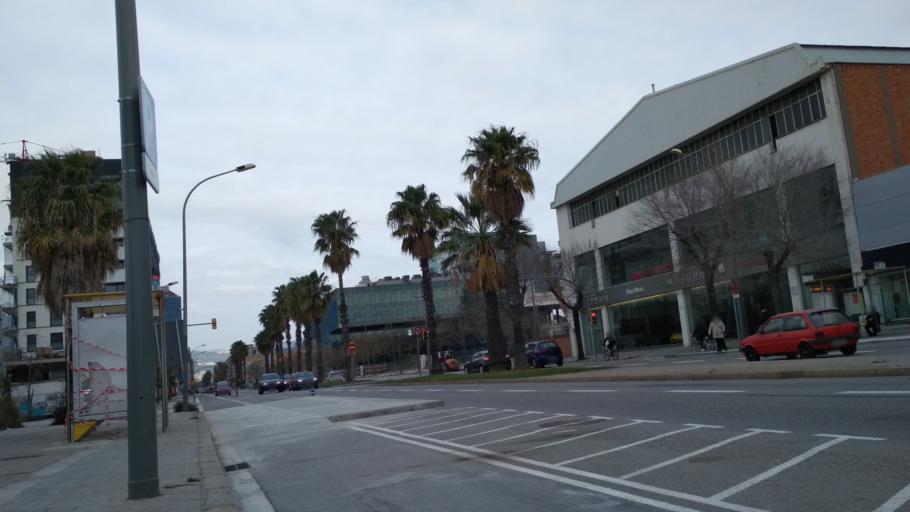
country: ES
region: Catalonia
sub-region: Provincia de Barcelona
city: Sants-Montjuic
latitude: 41.3515
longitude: 2.1452
